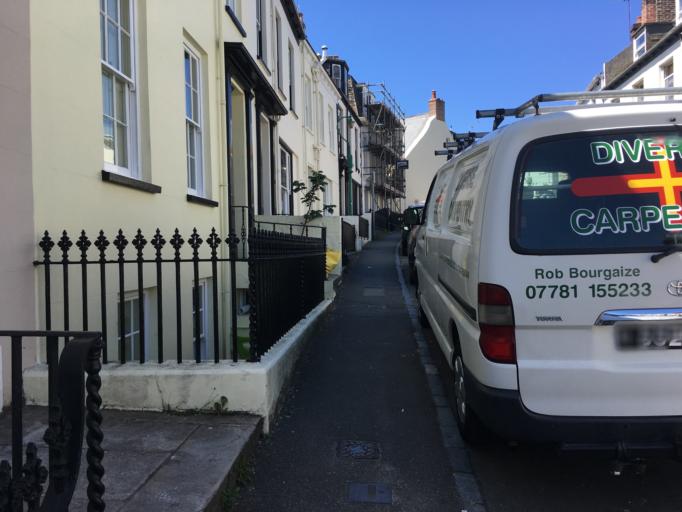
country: GG
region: St Peter Port
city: Saint Peter Port
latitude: 49.4549
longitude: -2.5466
